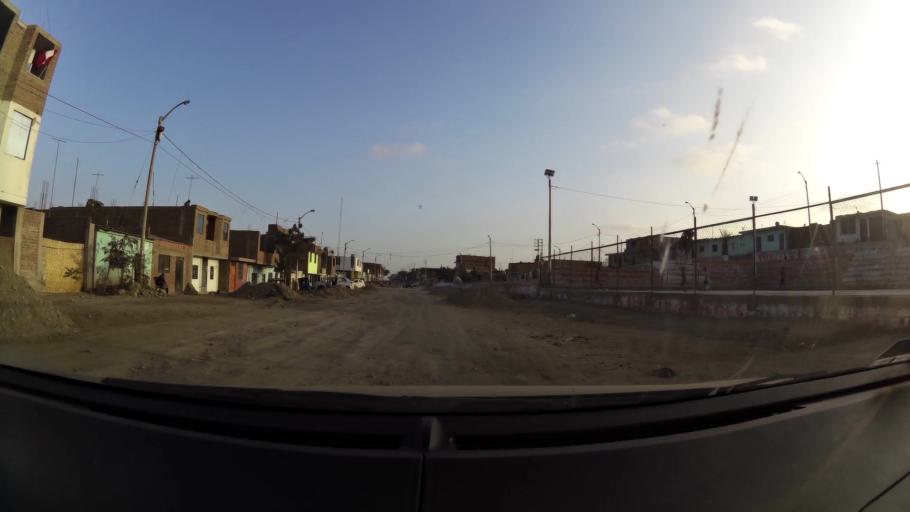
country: PE
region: La Libertad
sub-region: Provincia de Trujillo
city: El Porvenir
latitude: -8.0687
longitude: -78.9966
